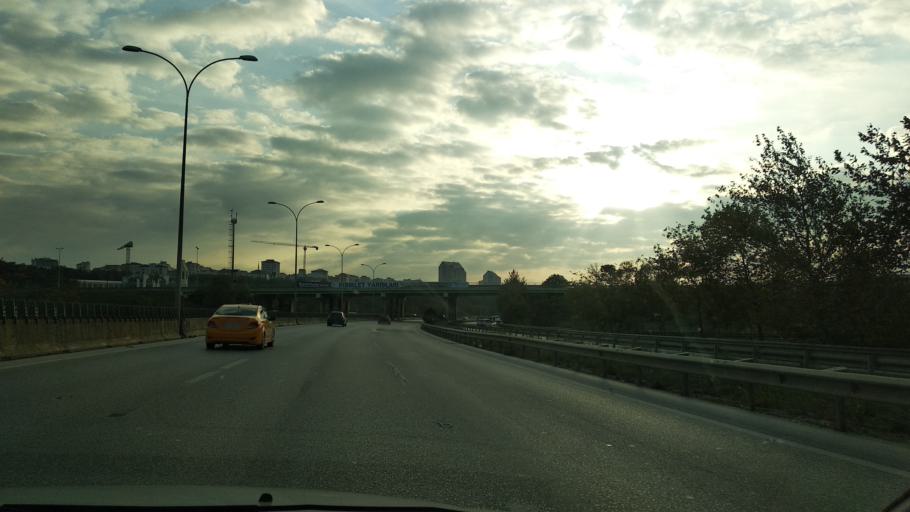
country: TR
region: Istanbul
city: Icmeler
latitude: 40.8800
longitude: 29.3154
